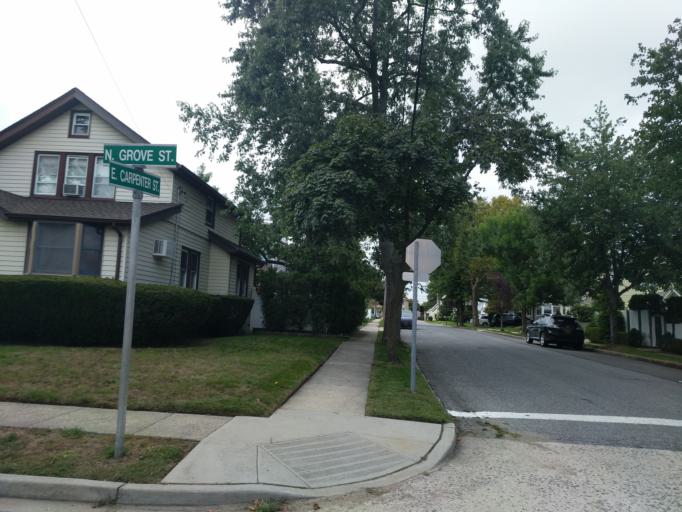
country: US
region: New York
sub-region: Nassau County
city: Valley Stream
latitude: 40.6677
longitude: -73.6949
